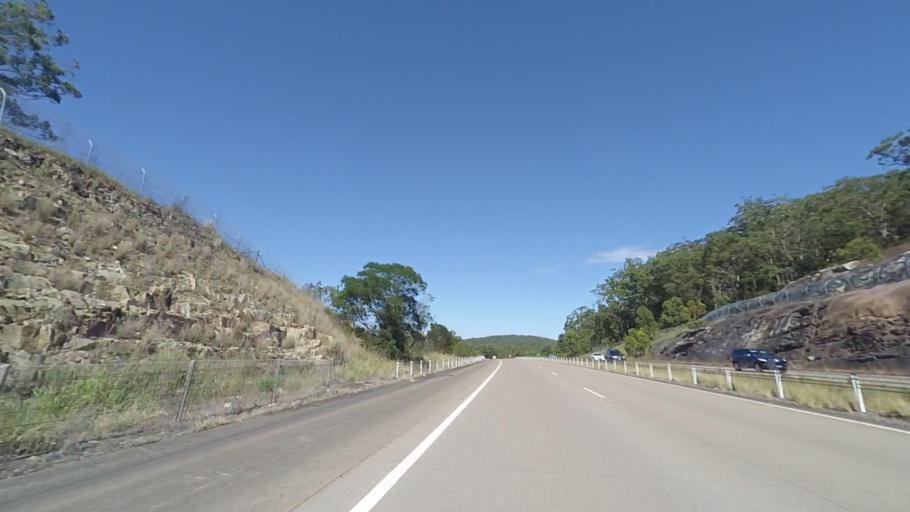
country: AU
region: New South Wales
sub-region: Port Stephens Shire
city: Port Stephens
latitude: -32.6205
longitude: 151.9690
